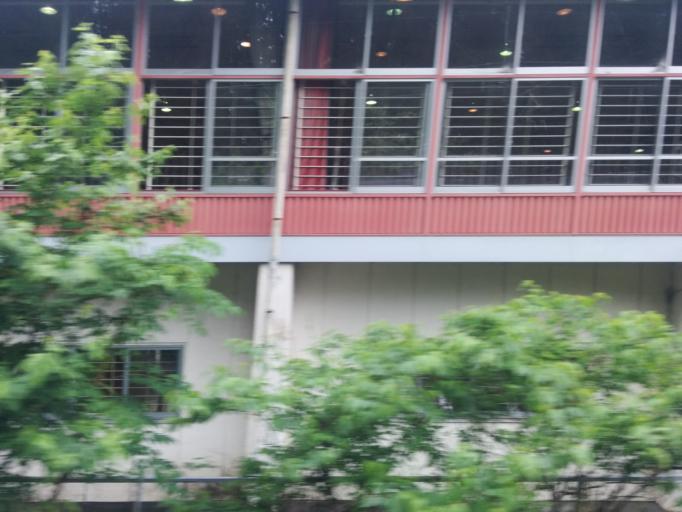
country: JP
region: Tochigi
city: Imaichi
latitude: 36.7177
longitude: 139.6926
